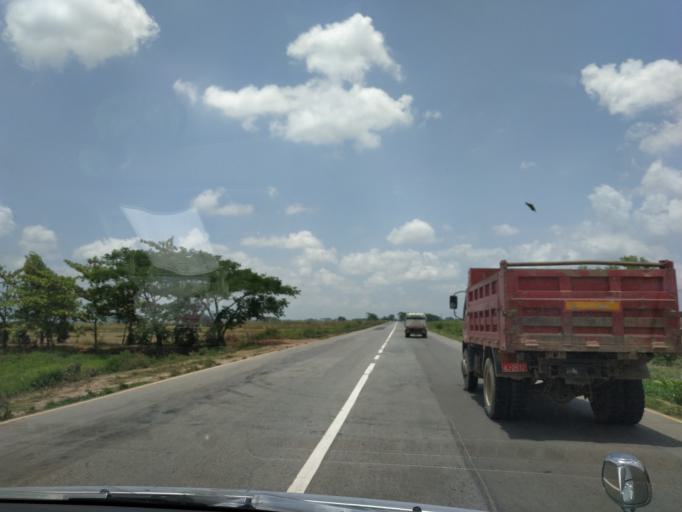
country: MM
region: Bago
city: Bago
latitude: 17.4645
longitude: 96.5891
